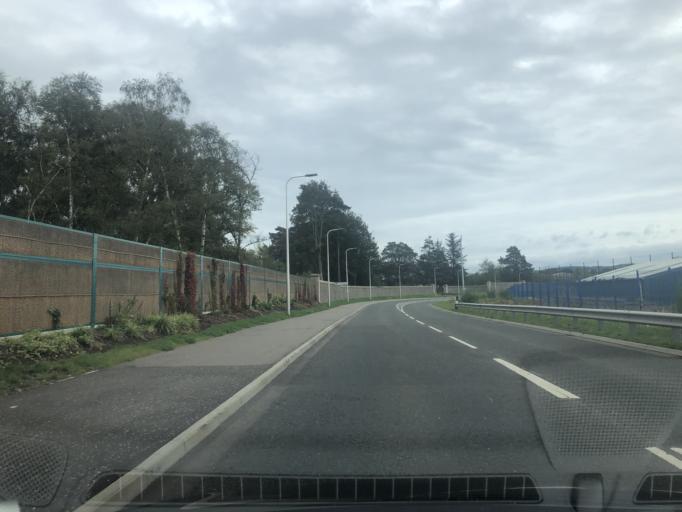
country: GB
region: Scotland
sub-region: Perth and Kinross
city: Luncarty
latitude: 56.4108
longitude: -3.4769
